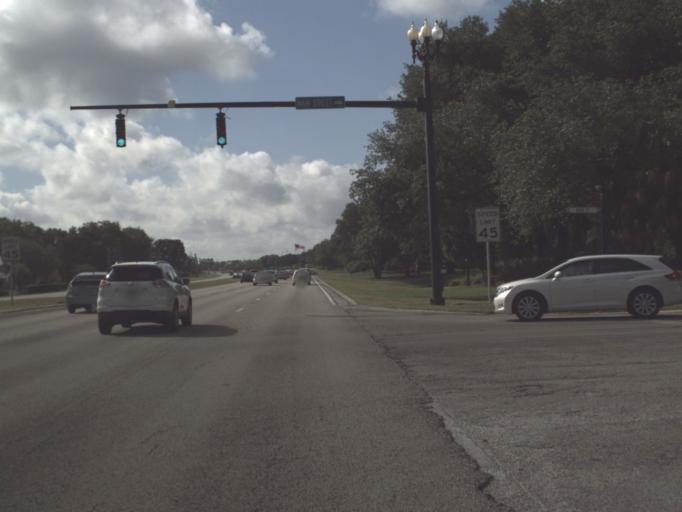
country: US
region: Florida
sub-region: Sumter County
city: The Villages
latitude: 28.9426
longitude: -81.9479
